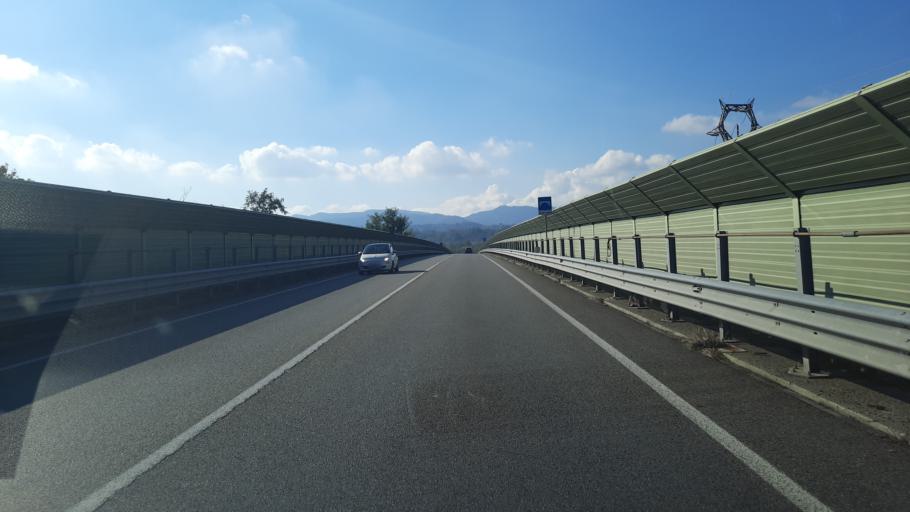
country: IT
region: Piedmont
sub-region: Provincia di Novara
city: Briga Novarese
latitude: 45.7240
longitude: 8.4554
